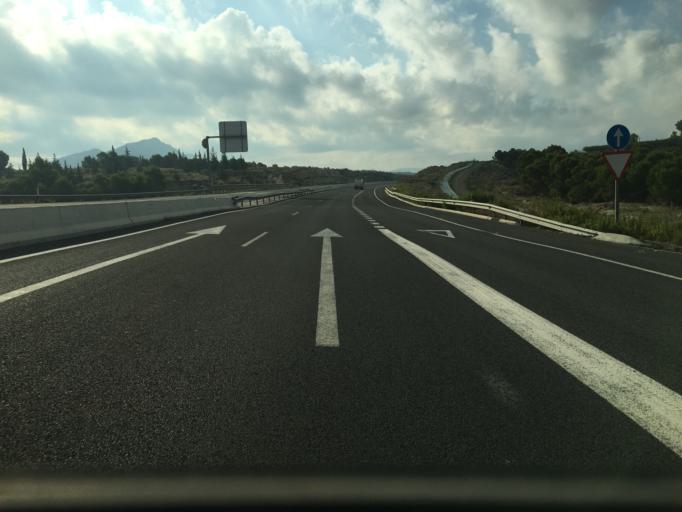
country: ES
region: Murcia
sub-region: Murcia
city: Beniel
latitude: 37.9961
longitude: -0.9816
